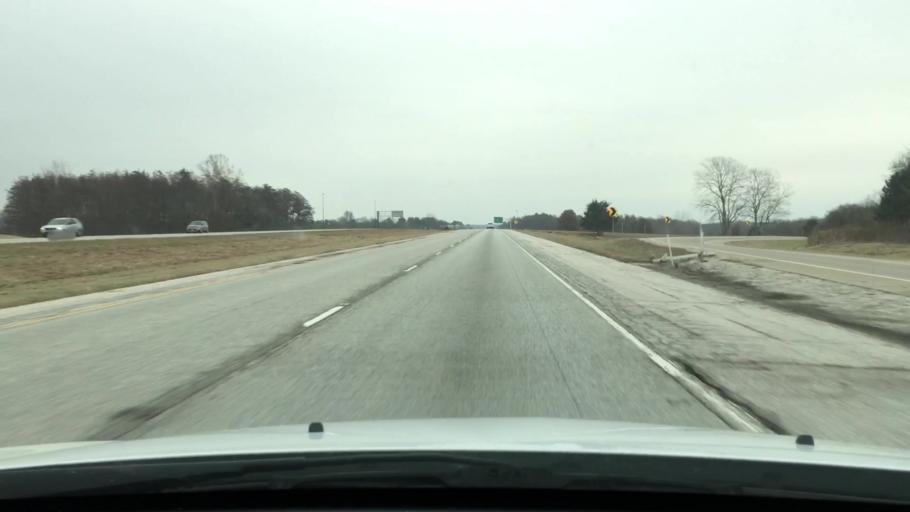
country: US
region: Illinois
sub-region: Morgan County
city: South Jacksonville
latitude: 39.6802
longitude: -90.3002
